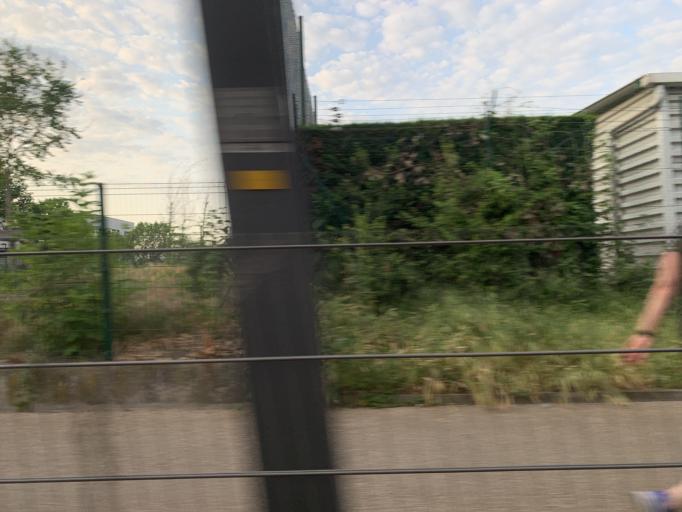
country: FR
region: Rhone-Alpes
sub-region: Departement du Rhone
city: Vaulx-en-Velin
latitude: 45.7591
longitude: 4.9147
